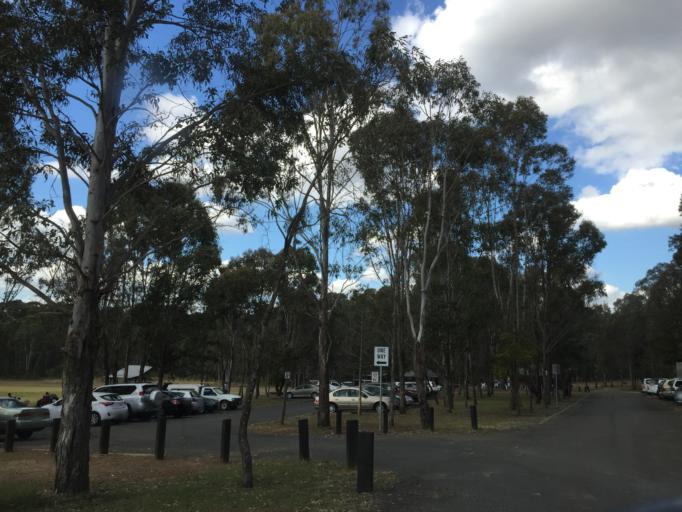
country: AU
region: New South Wales
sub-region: Blacktown
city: Rouse Hill
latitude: -33.6797
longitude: 150.9101
